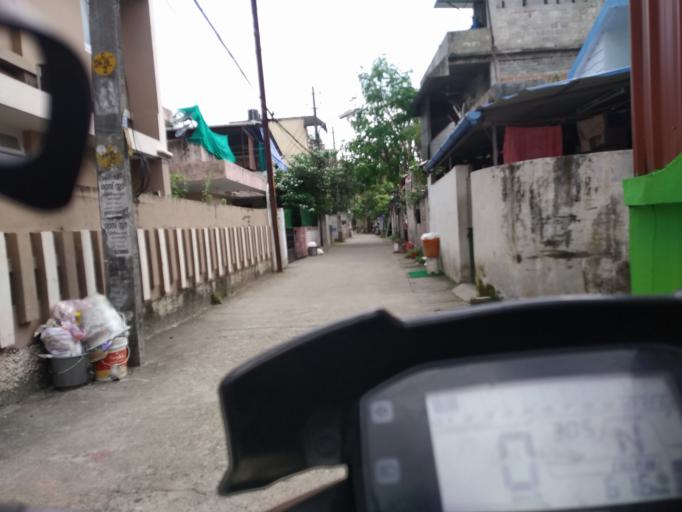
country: IN
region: Kerala
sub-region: Ernakulam
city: Cochin
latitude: 9.9899
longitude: 76.2841
